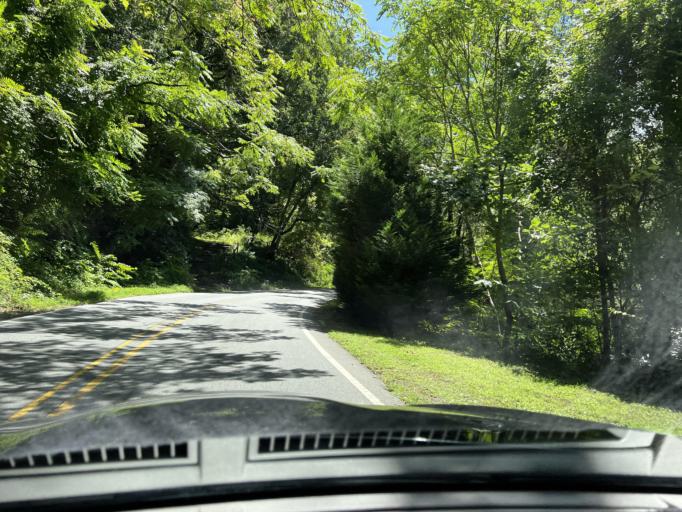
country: US
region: North Carolina
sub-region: Henderson County
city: Fruitland
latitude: 35.4269
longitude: -82.4208
